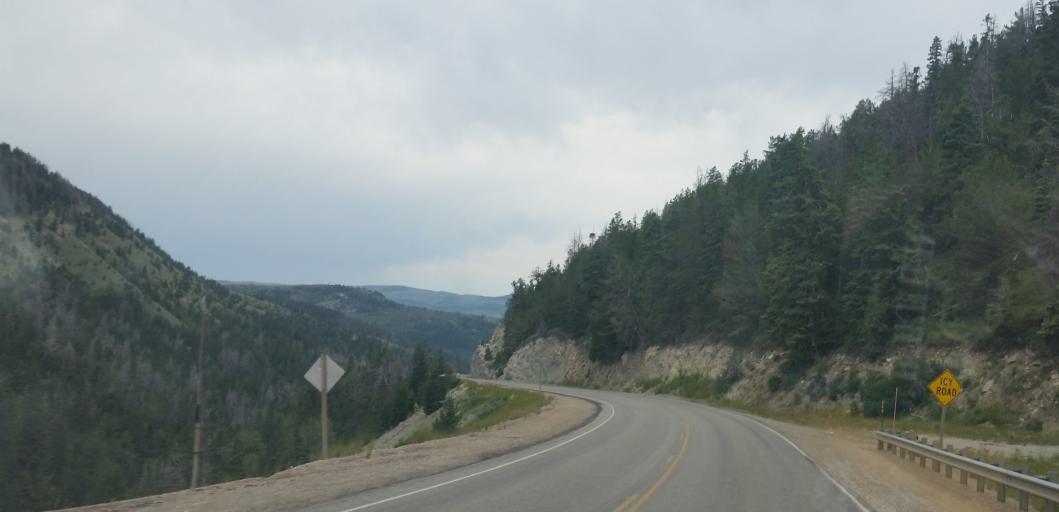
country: US
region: Utah
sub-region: Carbon County
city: Helper
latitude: 39.8750
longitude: -110.7624
